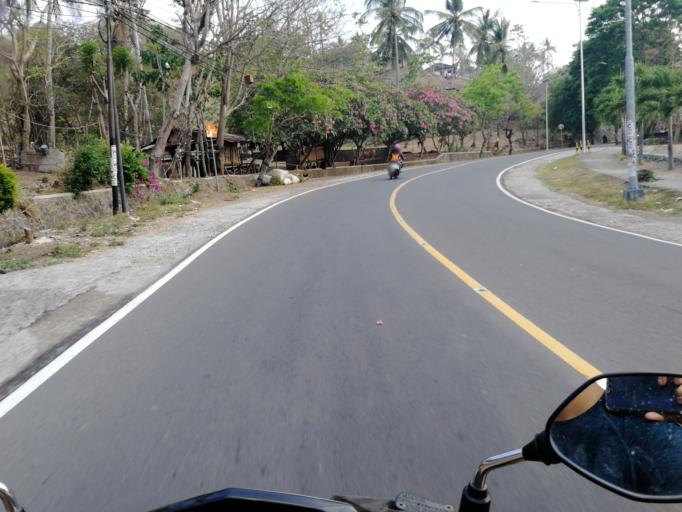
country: ID
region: West Nusa Tenggara
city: Mambalan
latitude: -8.4920
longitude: 116.0400
